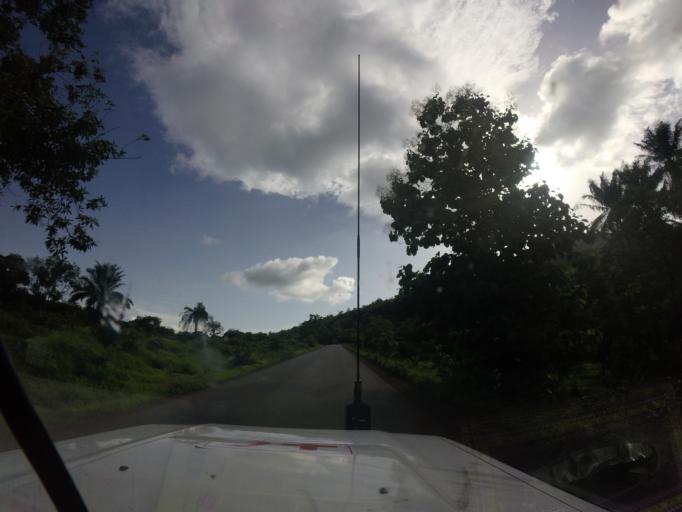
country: GN
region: Kindia
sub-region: Kindia
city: Kindia
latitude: 10.1449
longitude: -12.5405
